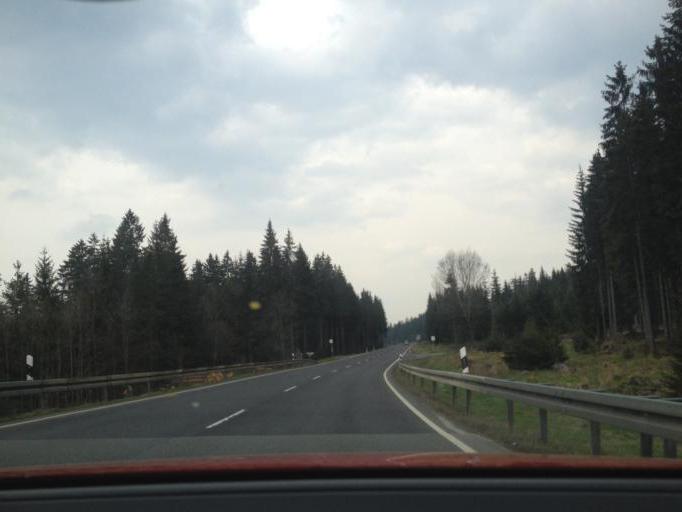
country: DE
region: Bavaria
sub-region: Upper Franconia
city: Fichtelberg
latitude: 50.0382
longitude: 11.8395
